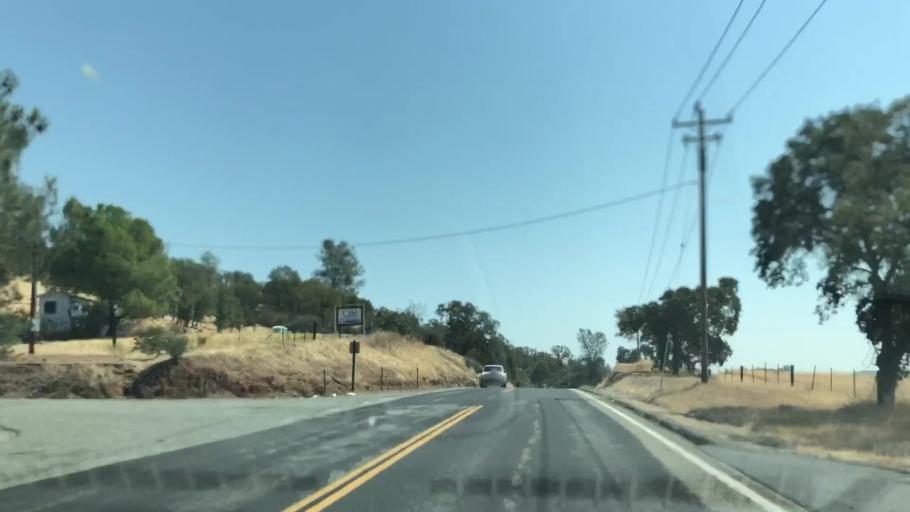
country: US
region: California
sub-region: Calaveras County
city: Copperopolis
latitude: 37.9234
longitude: -120.5947
